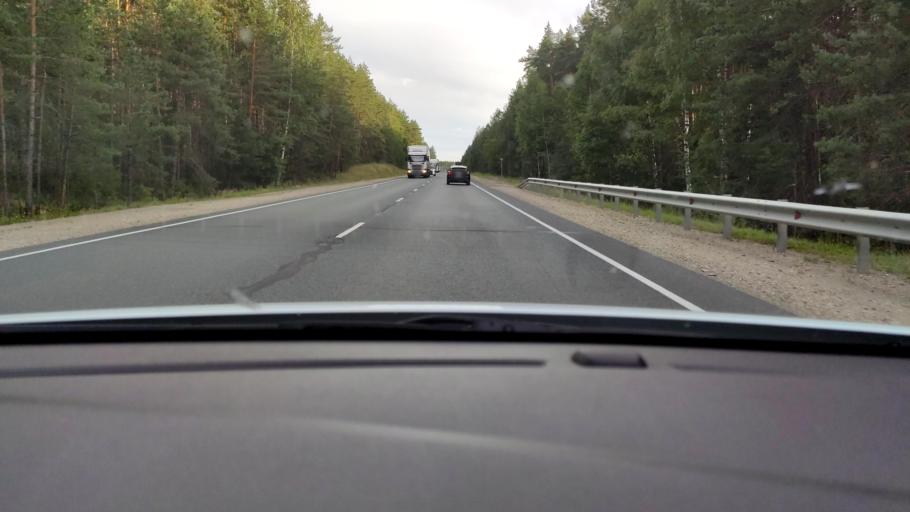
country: RU
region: Mariy-El
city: Pomary
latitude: 56.0395
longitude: 48.3788
